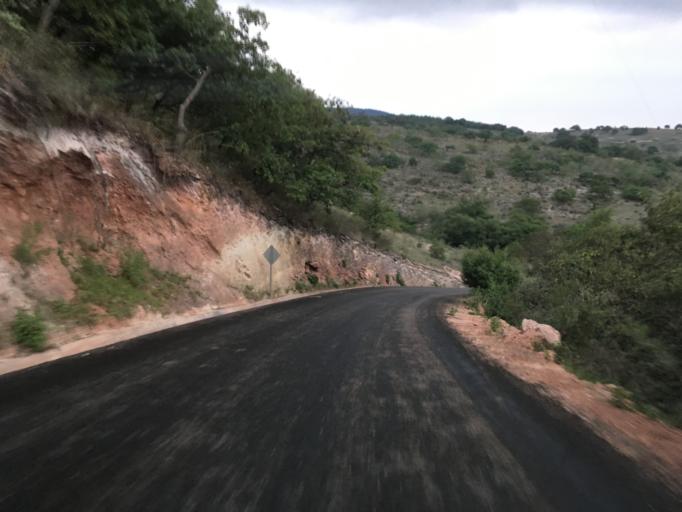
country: MX
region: Oaxaca
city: Magdalena Jaltepec
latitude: 17.2946
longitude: -97.2751
